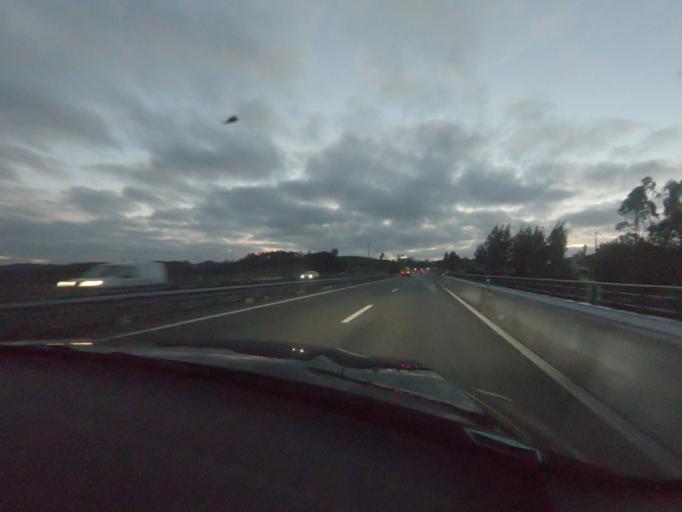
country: PT
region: Leiria
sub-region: Pombal
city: Pombal
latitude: 39.9721
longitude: -8.6448
